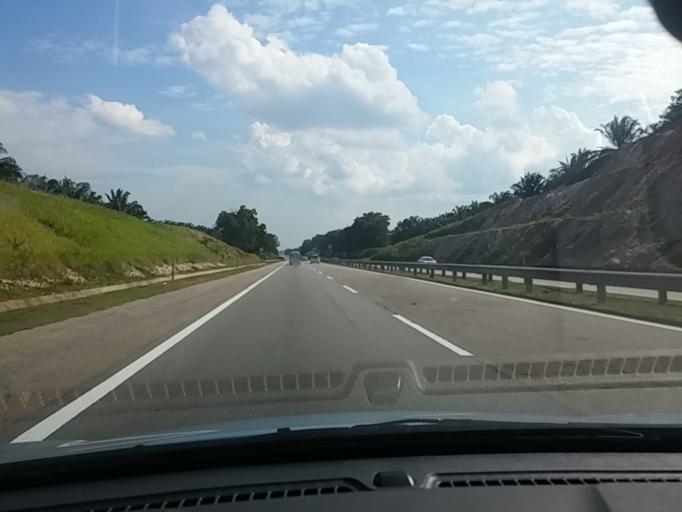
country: MY
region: Pahang
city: Temerluh
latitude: 3.5272
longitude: 102.4775
